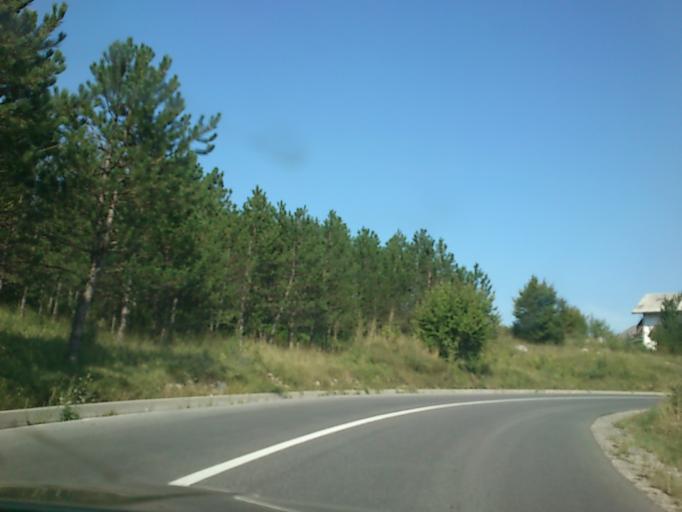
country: HR
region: Licko-Senjska
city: Otocac
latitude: 44.8566
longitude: 15.1572
